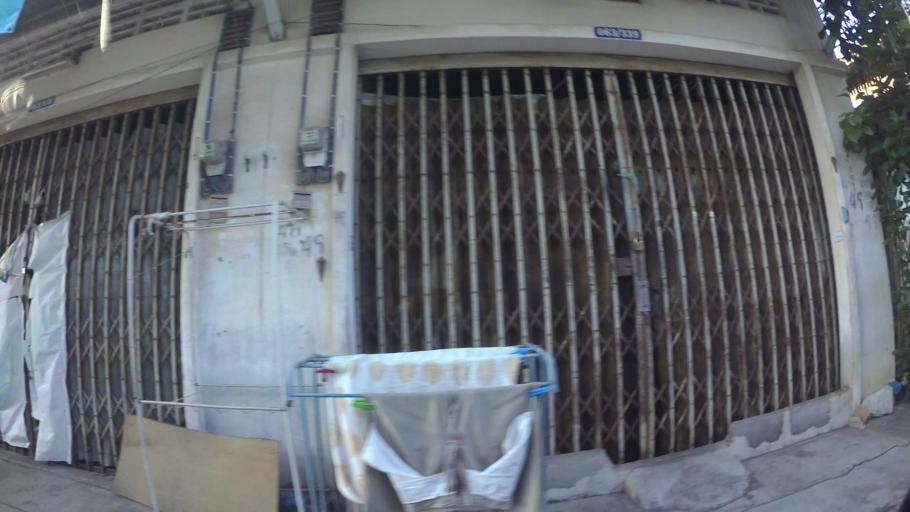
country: TH
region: Rayong
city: Rayong
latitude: 12.6850
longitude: 101.2790
